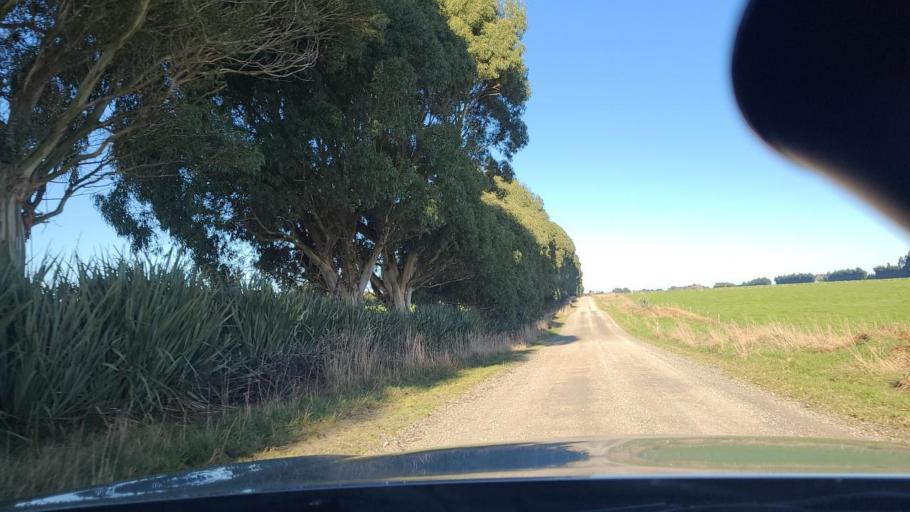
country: NZ
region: Southland
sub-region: Invercargill City
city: Invercargill
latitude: -46.2938
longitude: 168.6229
